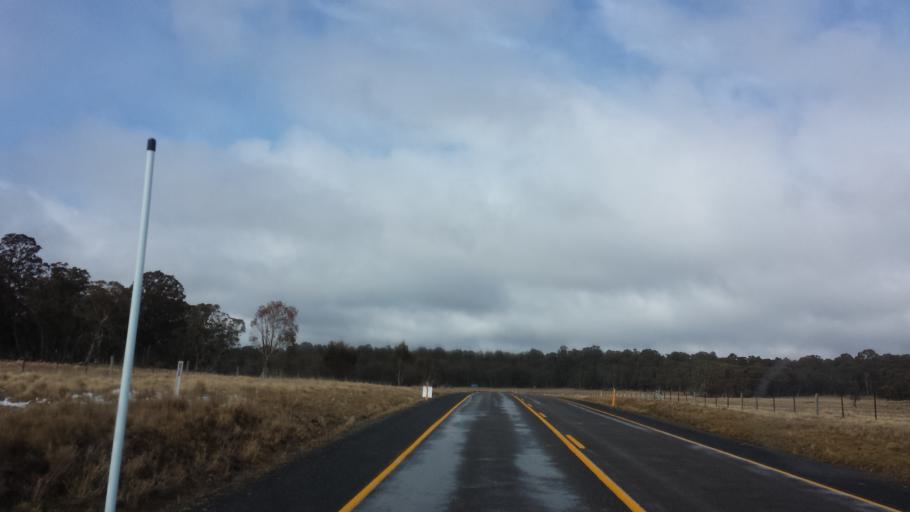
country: AU
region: Victoria
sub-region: Alpine
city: Mount Beauty
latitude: -37.0531
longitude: 147.3243
